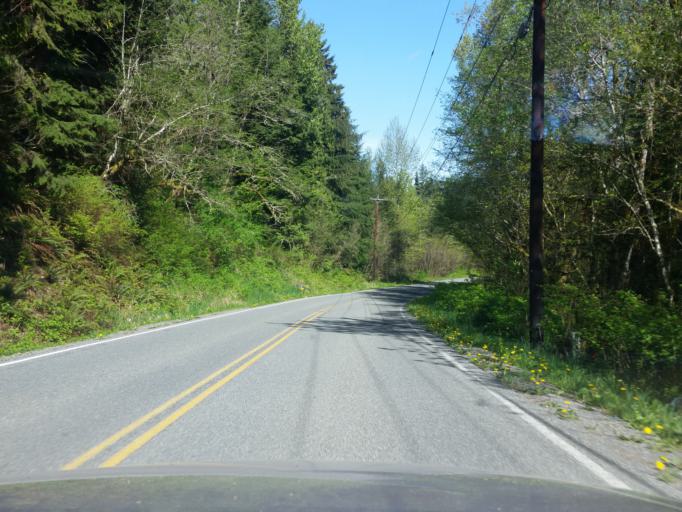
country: US
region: Washington
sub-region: Snohomish County
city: Granite Falls
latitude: 48.0160
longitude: -121.9190
